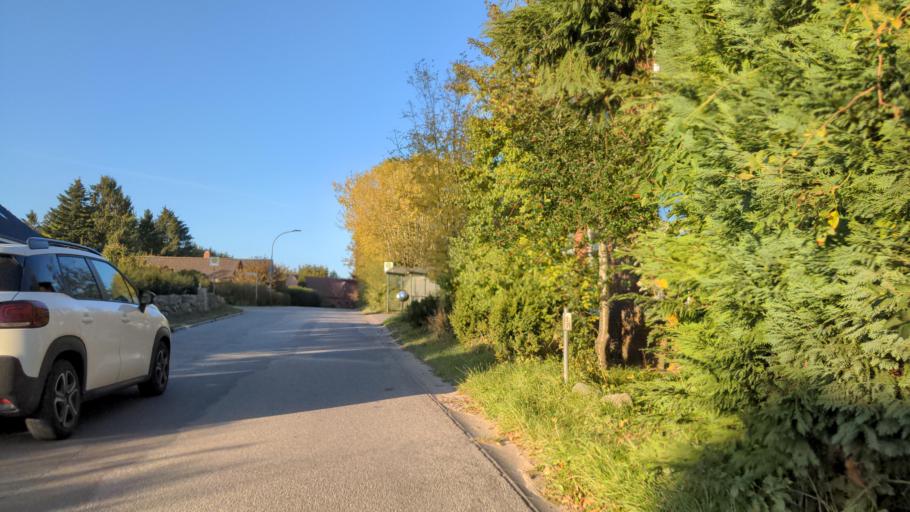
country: DE
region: Schleswig-Holstein
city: Ahrensbok
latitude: 53.9657
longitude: 10.5335
